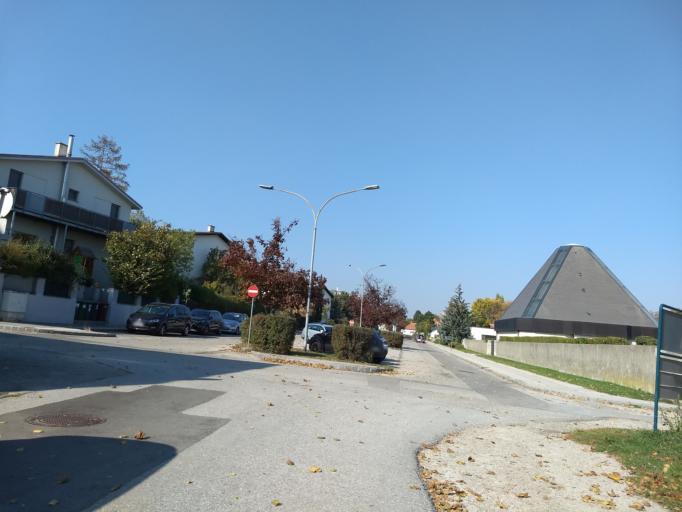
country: AT
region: Lower Austria
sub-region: Politischer Bezirk Modling
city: Perchtoldsdorf
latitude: 48.1161
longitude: 16.2747
